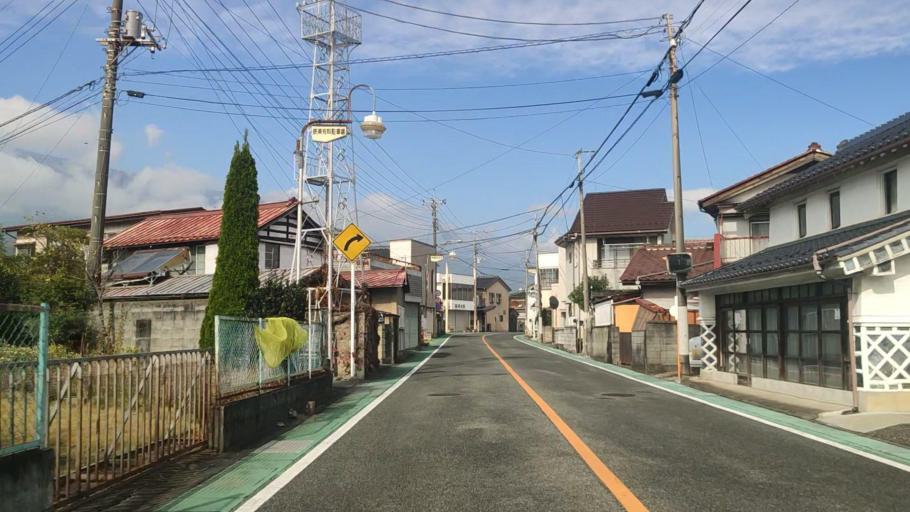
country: JP
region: Yamanashi
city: Ryuo
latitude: 35.5626
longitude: 138.4664
